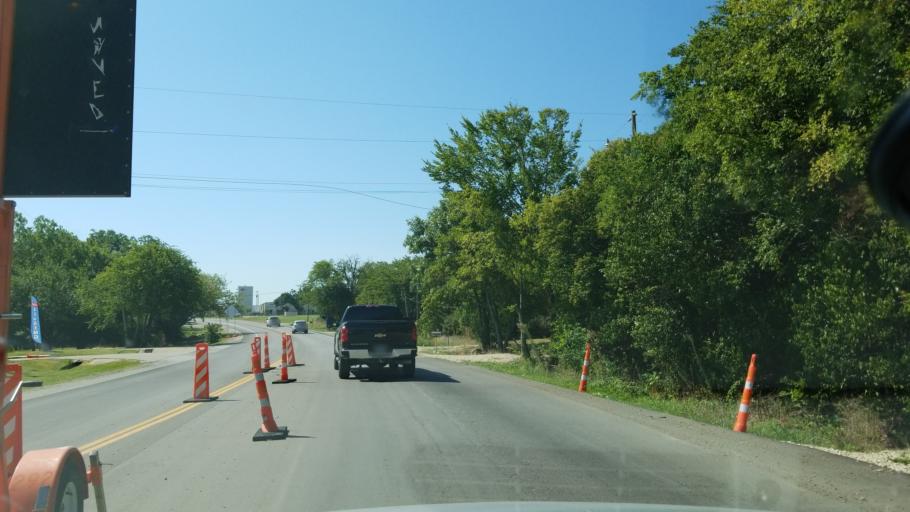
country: US
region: Texas
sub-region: Tarrant County
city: Mansfield
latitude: 32.5582
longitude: -97.1421
